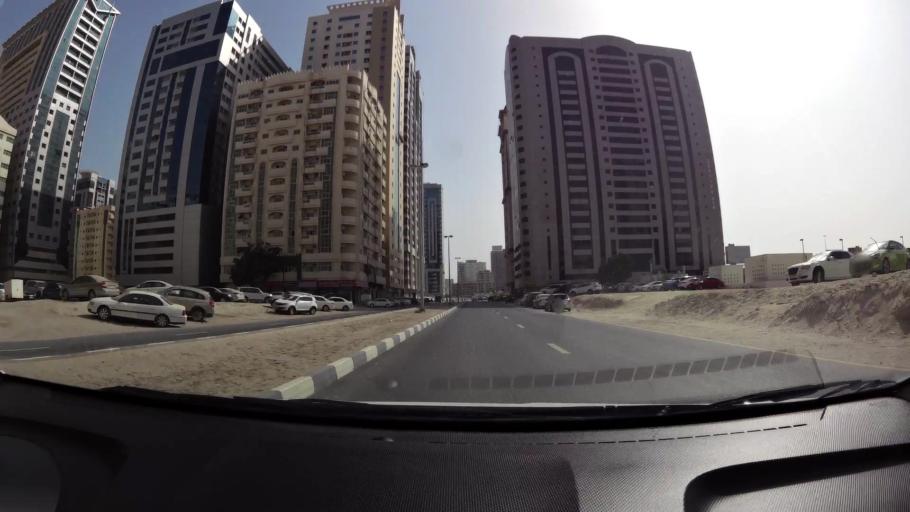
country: AE
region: Ash Shariqah
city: Sharjah
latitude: 25.3113
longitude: 55.3776
